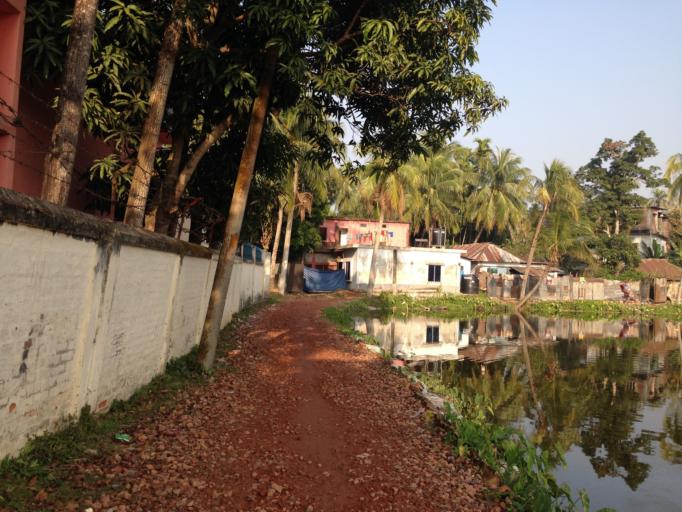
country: BD
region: Chittagong
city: Lakshmipur
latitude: 22.9353
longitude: 90.8269
